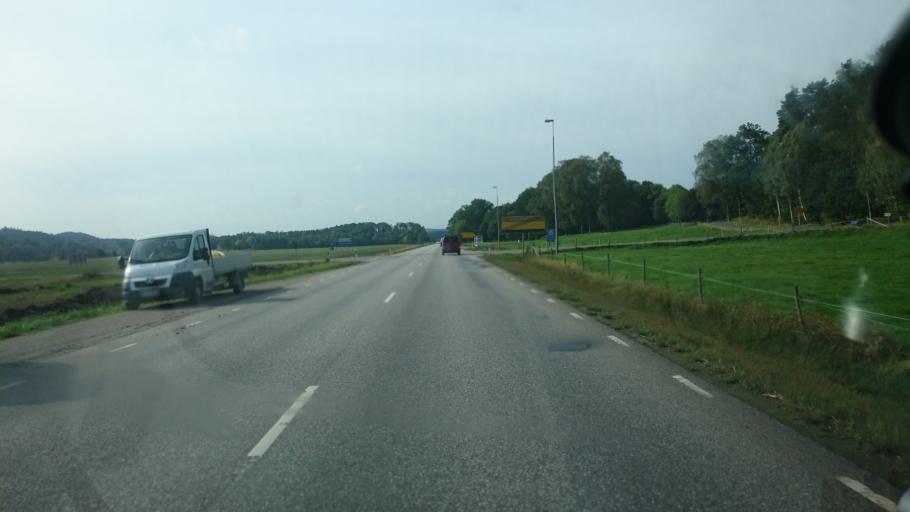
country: SE
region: Vaestra Goetaland
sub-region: Alingsas Kommun
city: Sollebrunn
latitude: 58.1104
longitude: 12.5240
